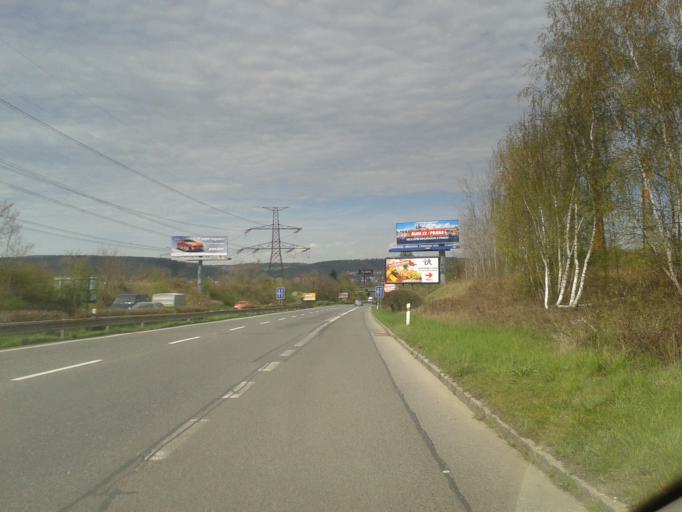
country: CZ
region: Central Bohemia
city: Vrane nad Vltavou
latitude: 49.9622
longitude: 14.3781
